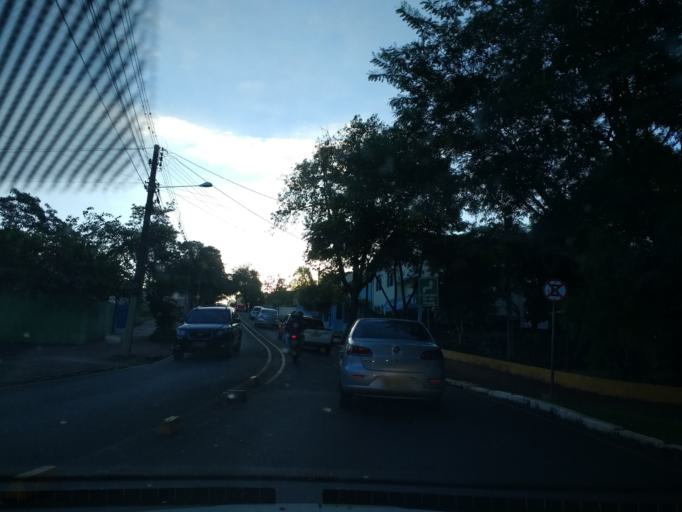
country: BR
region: Parana
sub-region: Londrina
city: Londrina
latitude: -23.3270
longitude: -51.1645
